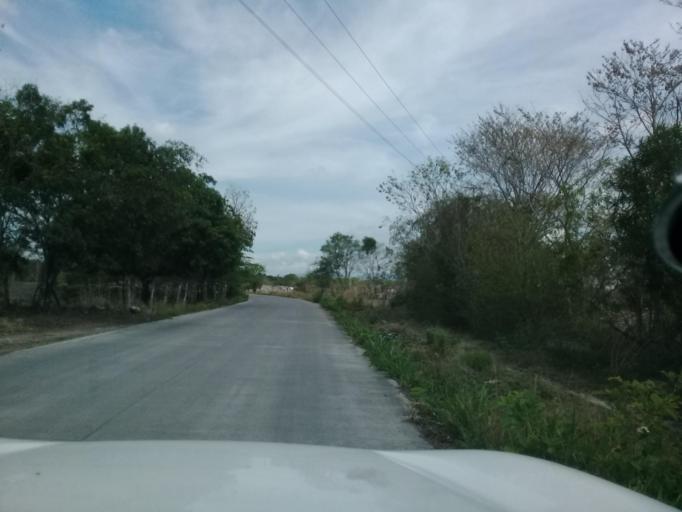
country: MX
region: Veracruz
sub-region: Emiliano Zapata
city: Plan del Rio
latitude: 19.3529
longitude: -96.6394
